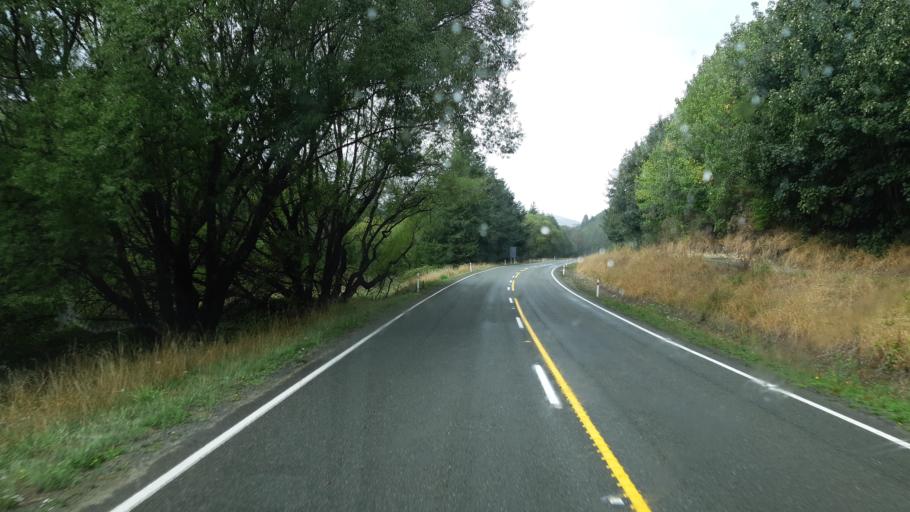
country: NZ
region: Tasman
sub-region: Tasman District
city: Wakefield
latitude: -41.4757
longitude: 172.8574
